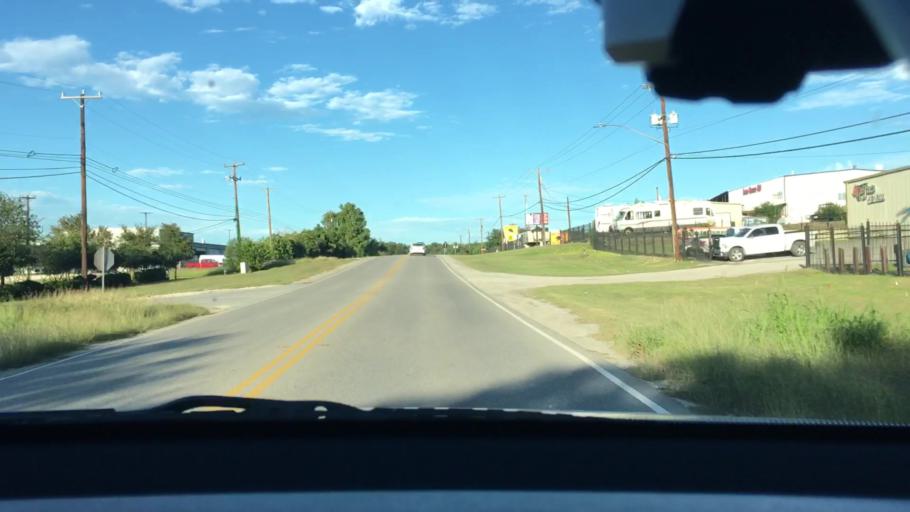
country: US
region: Texas
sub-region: Bexar County
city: Live Oak
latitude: 29.5454
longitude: -98.3637
